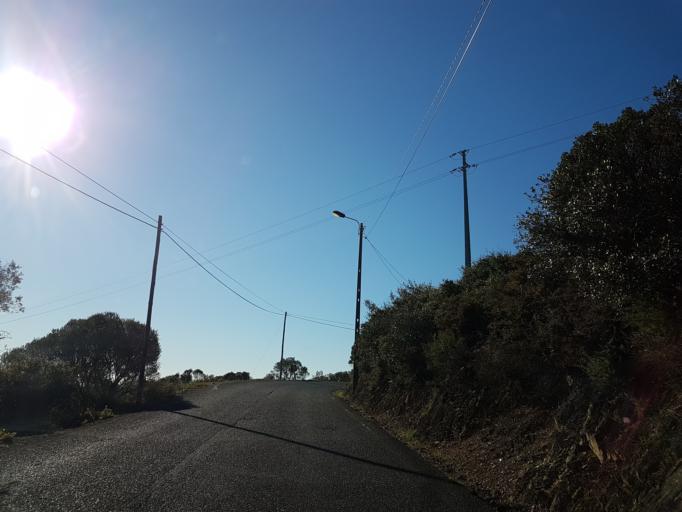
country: PT
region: Lisbon
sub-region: Cascais
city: Alcabideche
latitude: 38.7482
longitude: -9.4324
